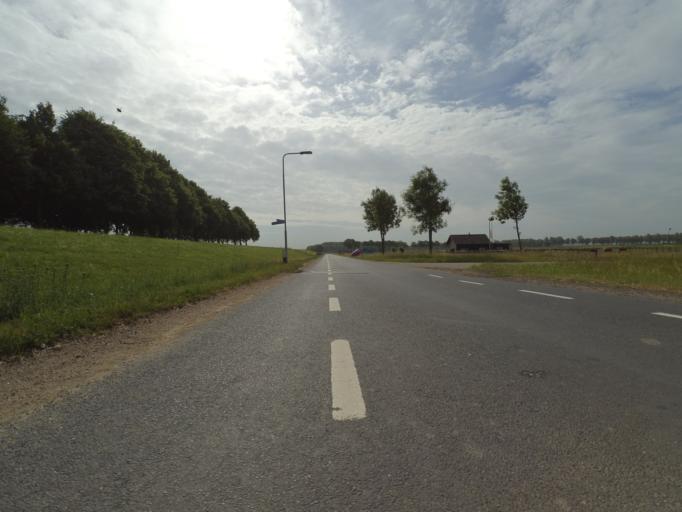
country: NL
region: Utrecht
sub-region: Gemeente Wijk bij Duurstede
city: Wijk bij Duurstede
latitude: 51.9524
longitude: 5.3572
